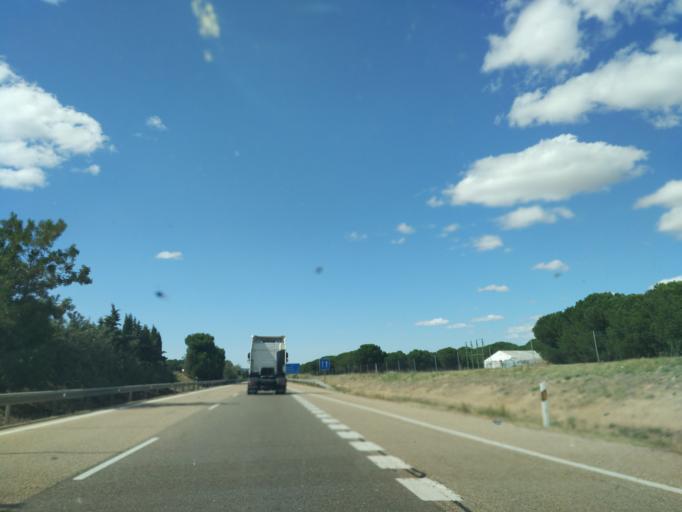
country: ES
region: Castille and Leon
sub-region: Provincia de Valladolid
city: Rueda
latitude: 41.4473
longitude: -4.9783
